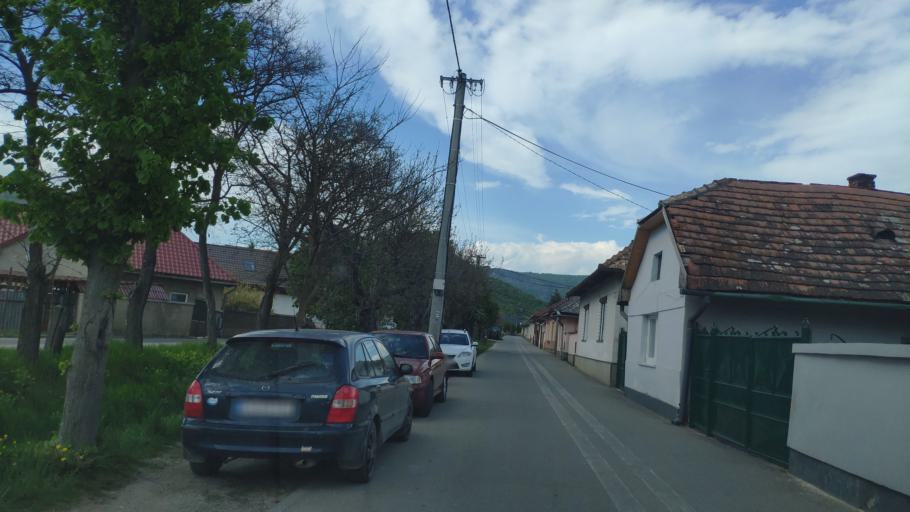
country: SK
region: Kosicky
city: Medzev
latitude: 48.5979
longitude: 20.8782
